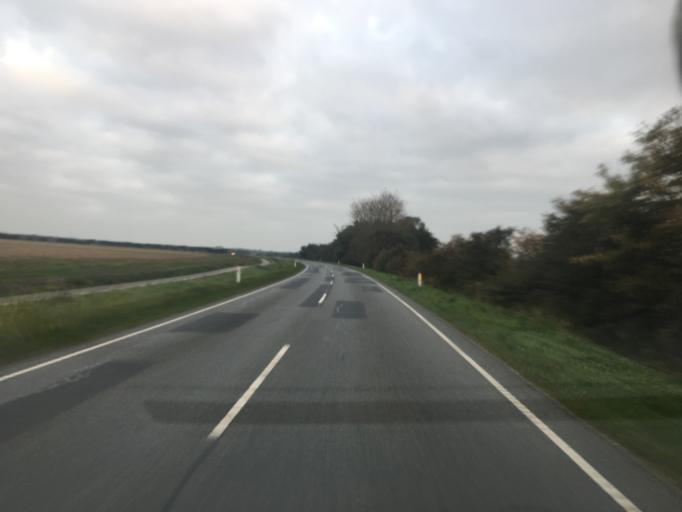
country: DE
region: Schleswig-Holstein
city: Aventoft
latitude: 54.9496
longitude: 8.8076
